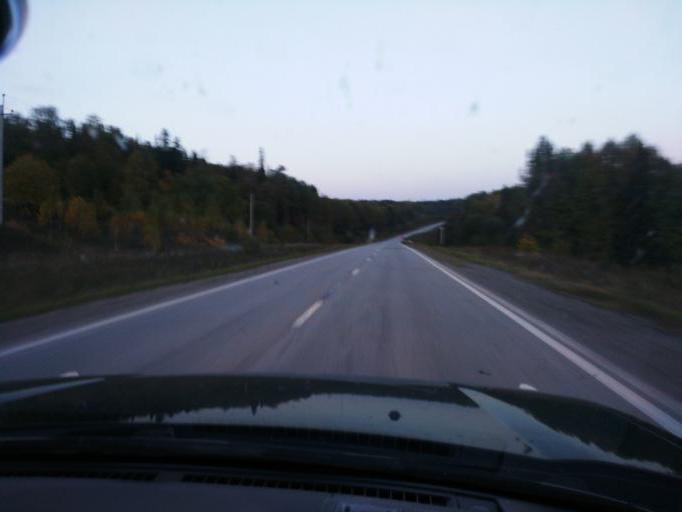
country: RU
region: Perm
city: Verkhnechusovskiye Gorodki
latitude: 58.2809
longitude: 56.9142
